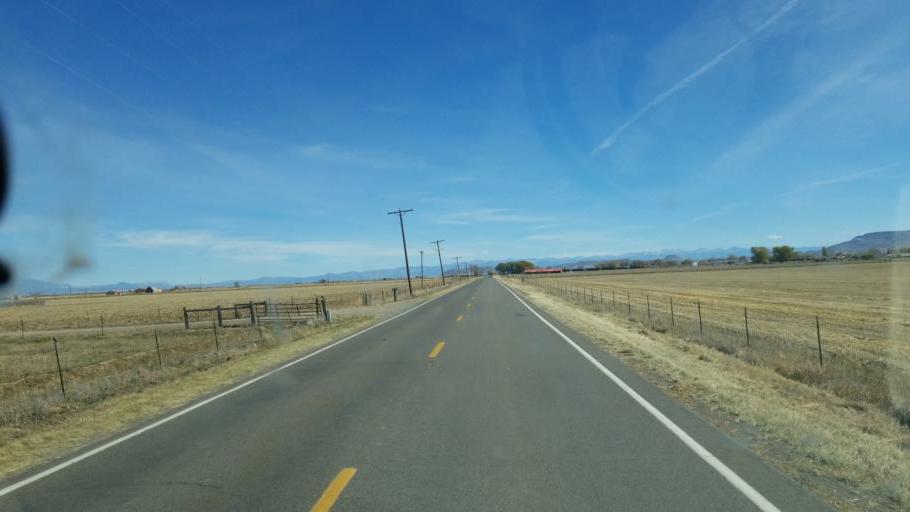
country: US
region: Colorado
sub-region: Conejos County
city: Conejos
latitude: 37.2836
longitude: -105.9697
